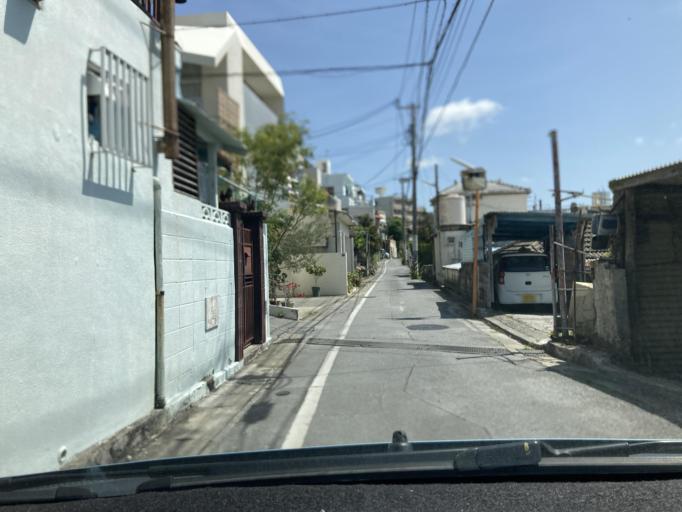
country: JP
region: Okinawa
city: Tomigusuku
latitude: 26.1993
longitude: 127.6895
